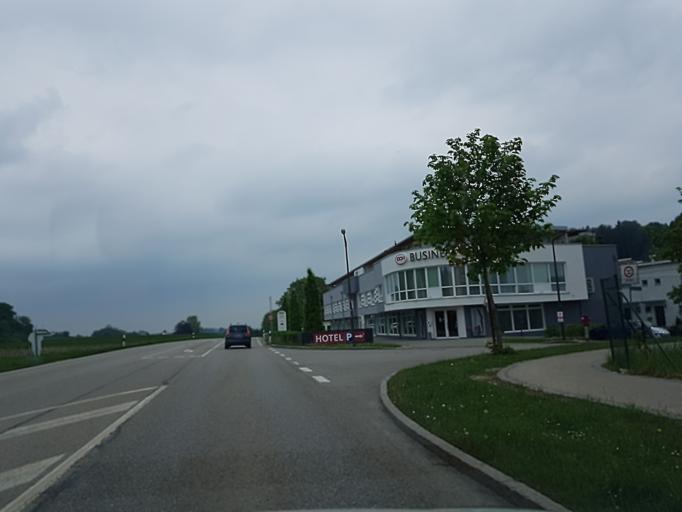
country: DE
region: Bavaria
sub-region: Upper Bavaria
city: Ebersberg
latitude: 48.0948
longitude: 11.9648
